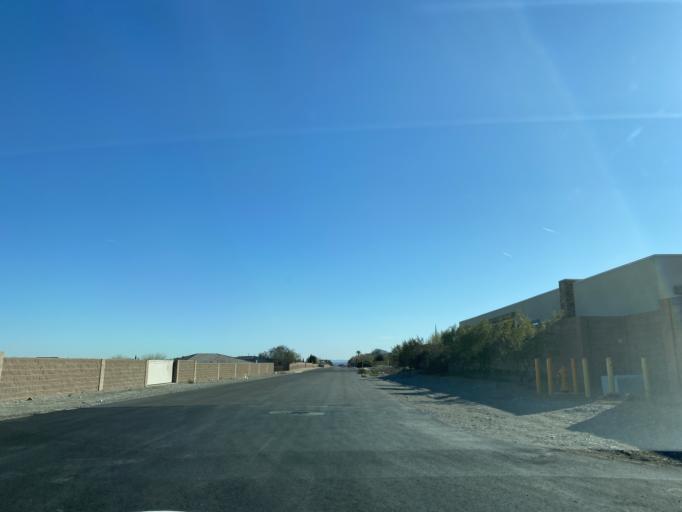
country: US
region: Nevada
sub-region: Clark County
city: Summerlin South
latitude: 36.2950
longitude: -115.3103
